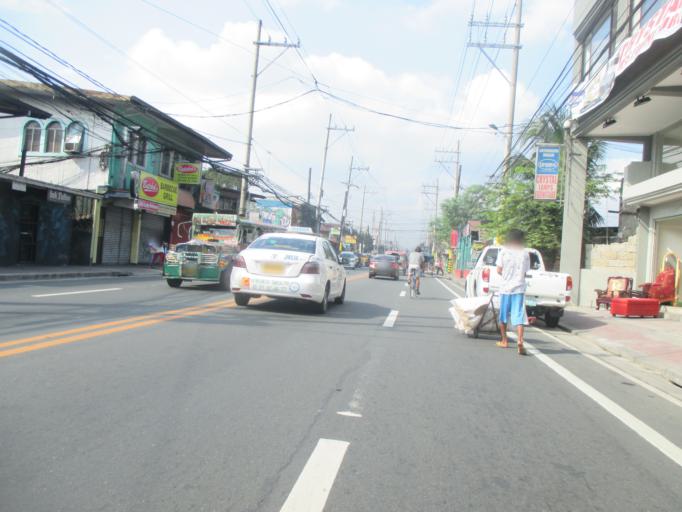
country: PH
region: Metro Manila
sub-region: Marikina
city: Calumpang
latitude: 14.6357
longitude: 121.0895
